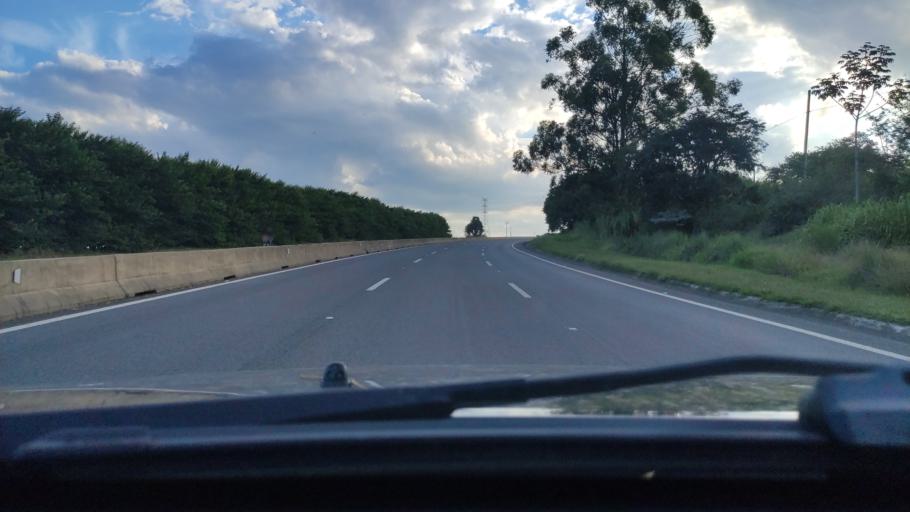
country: BR
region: Sao Paulo
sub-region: Mogi-Mirim
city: Mogi Mirim
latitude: -22.4489
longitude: -47.0592
